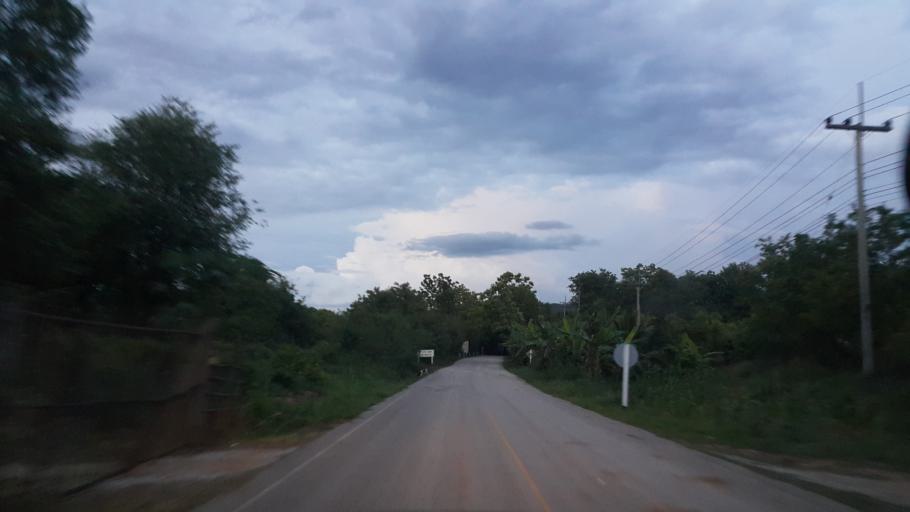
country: TH
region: Loei
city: Phu Ruea
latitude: 17.5328
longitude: 101.2255
